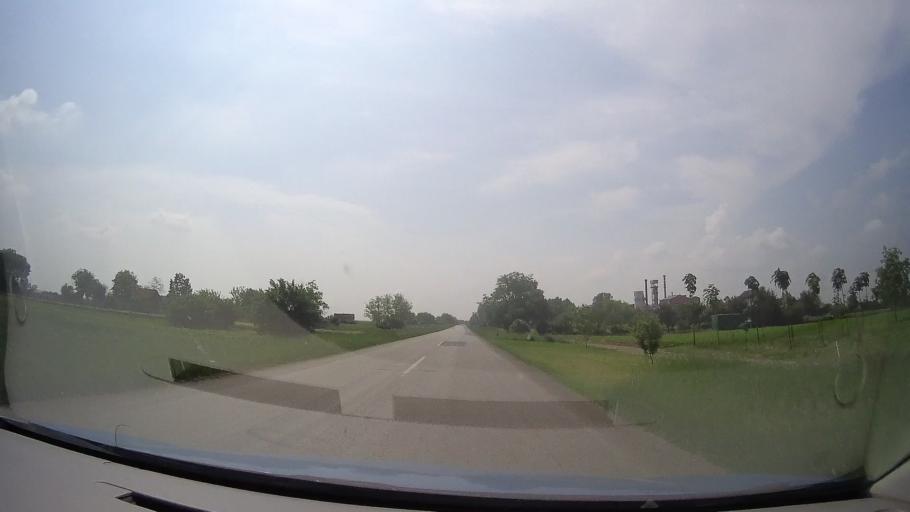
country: RS
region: Autonomna Pokrajina Vojvodina
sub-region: Juznobanatski Okrug
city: Kovacica
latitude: 45.0909
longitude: 20.6335
